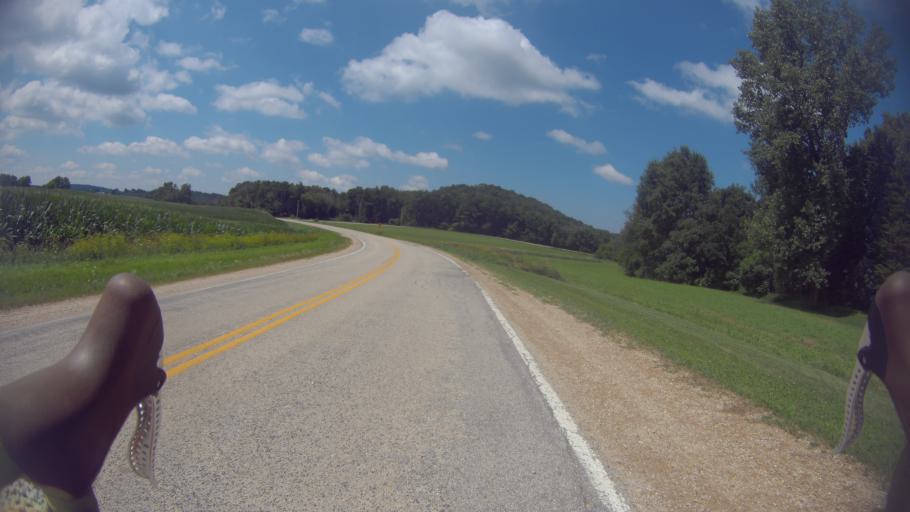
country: US
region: Wisconsin
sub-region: Sauk County
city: Sauk City
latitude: 43.2453
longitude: -89.6319
